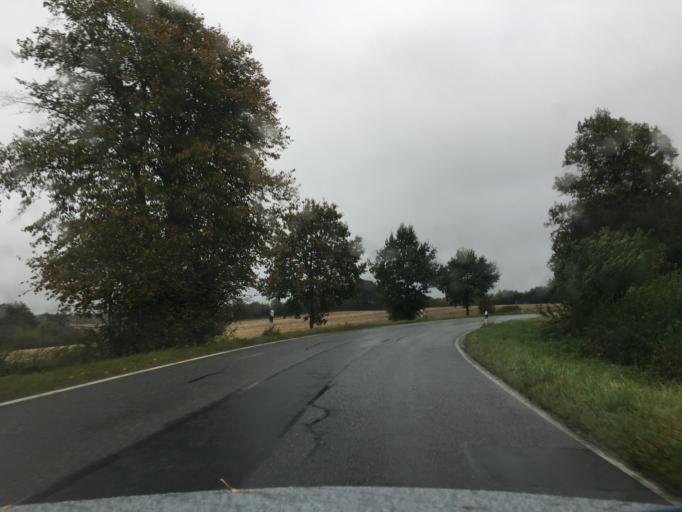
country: DE
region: Schleswig-Holstein
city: Melsdorf
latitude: 54.3100
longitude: 10.0352
